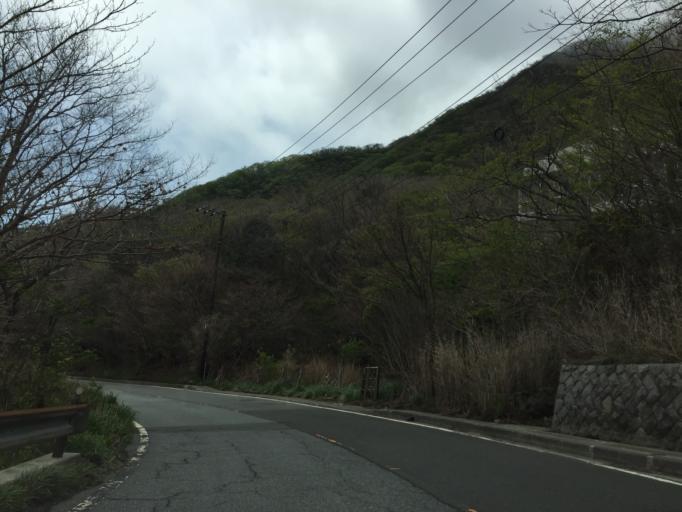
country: JP
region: Kanagawa
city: Hakone
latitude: 35.2486
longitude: 139.0289
